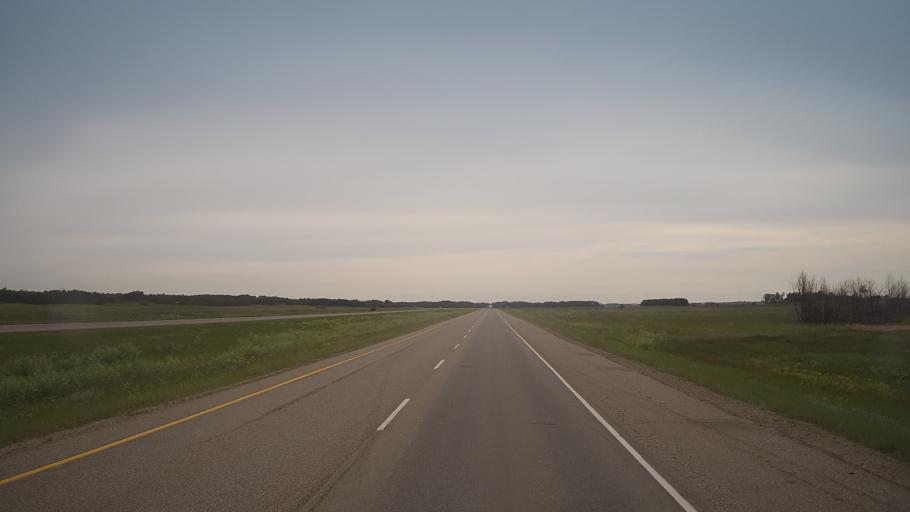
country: CA
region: Saskatchewan
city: Saskatoon
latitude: 51.8598
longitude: -106.5073
